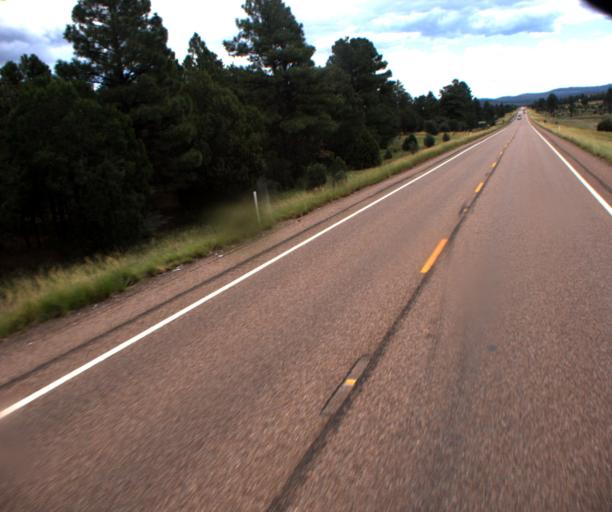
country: US
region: Arizona
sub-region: Navajo County
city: Linden
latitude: 34.3323
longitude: -110.2674
